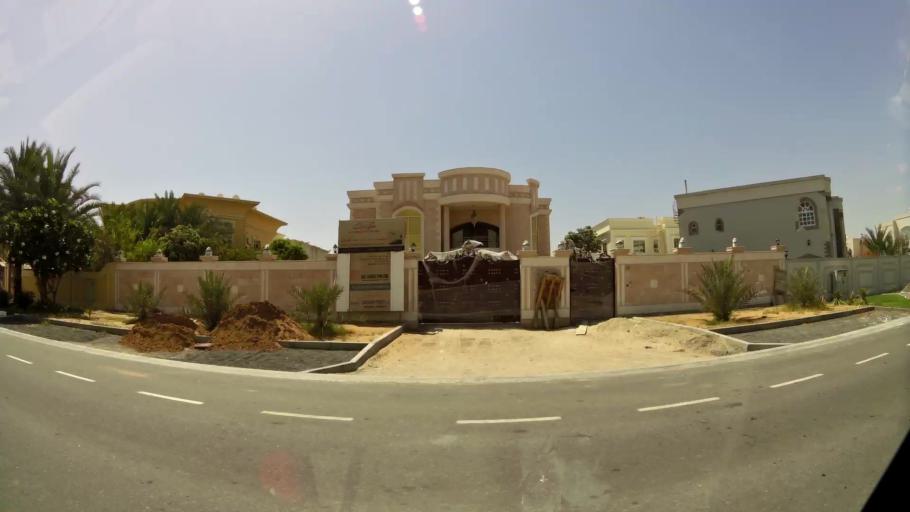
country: AE
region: Dubai
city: Dubai
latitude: 25.1088
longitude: 55.2106
